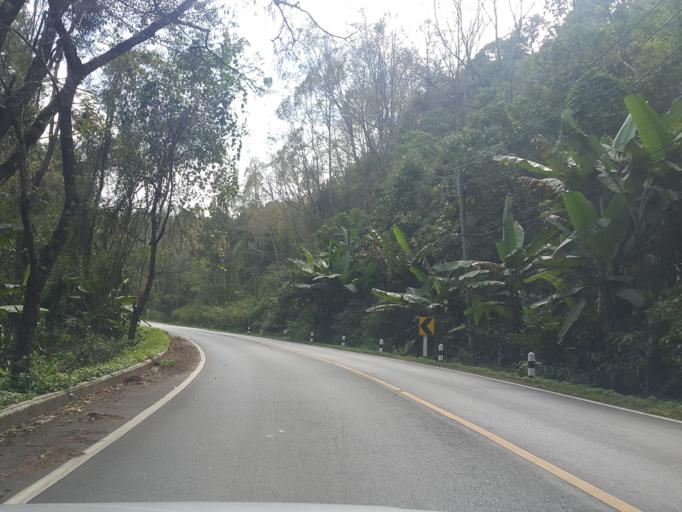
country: TH
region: Chiang Mai
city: Mae Chaem
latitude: 18.5132
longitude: 98.5134
